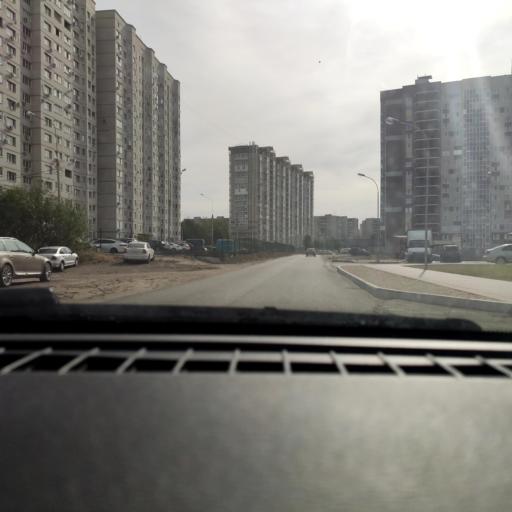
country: RU
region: Voronezj
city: Voronezh
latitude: 51.7157
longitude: 39.2688
